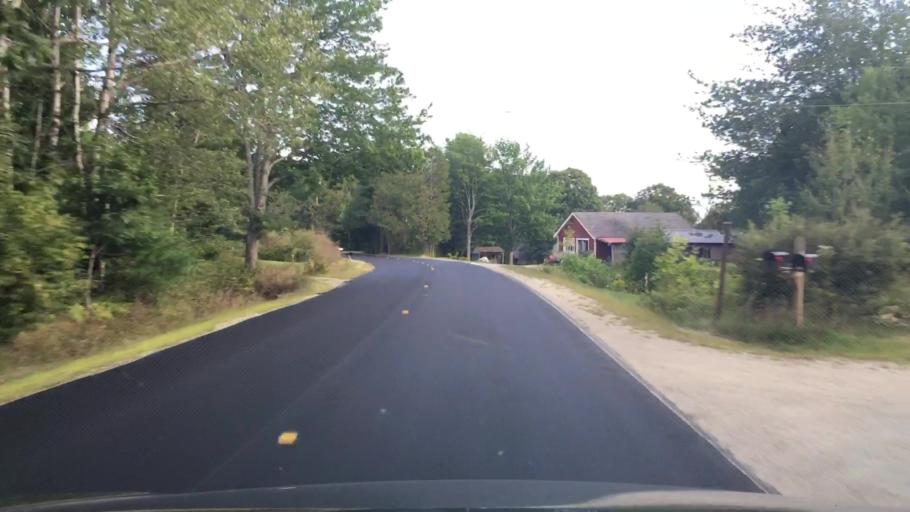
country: US
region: Maine
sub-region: Hancock County
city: Orland
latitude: 44.5462
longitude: -68.6201
